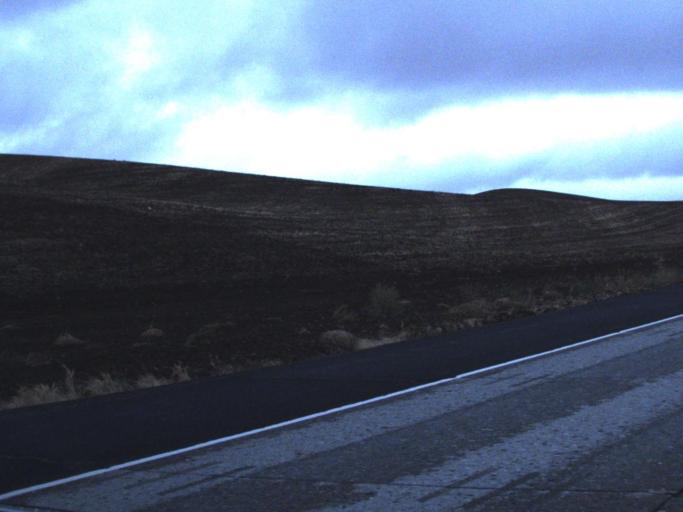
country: US
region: Washington
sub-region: Whitman County
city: Colfax
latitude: 47.0370
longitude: -117.3690
